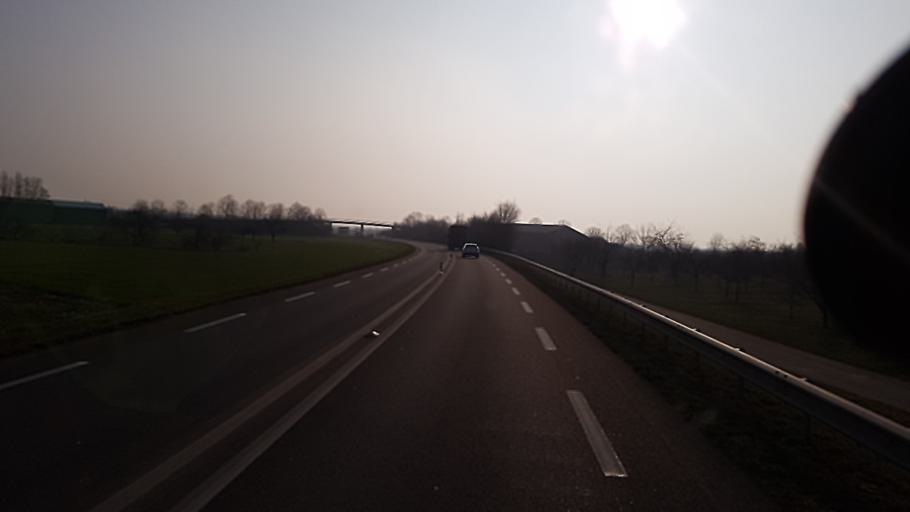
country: FR
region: Alsace
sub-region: Departement du Bas-Rhin
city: Dorlisheim
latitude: 48.5194
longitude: 7.4718
